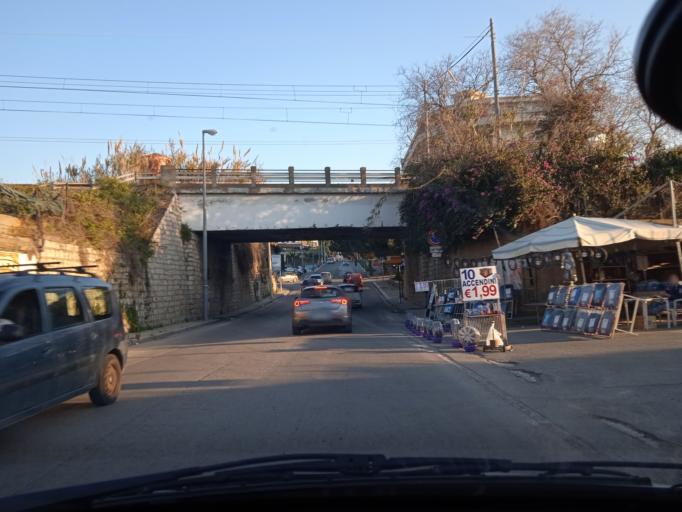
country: IT
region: Sicily
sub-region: Palermo
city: Bagheria
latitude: 38.0880
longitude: 13.5007
